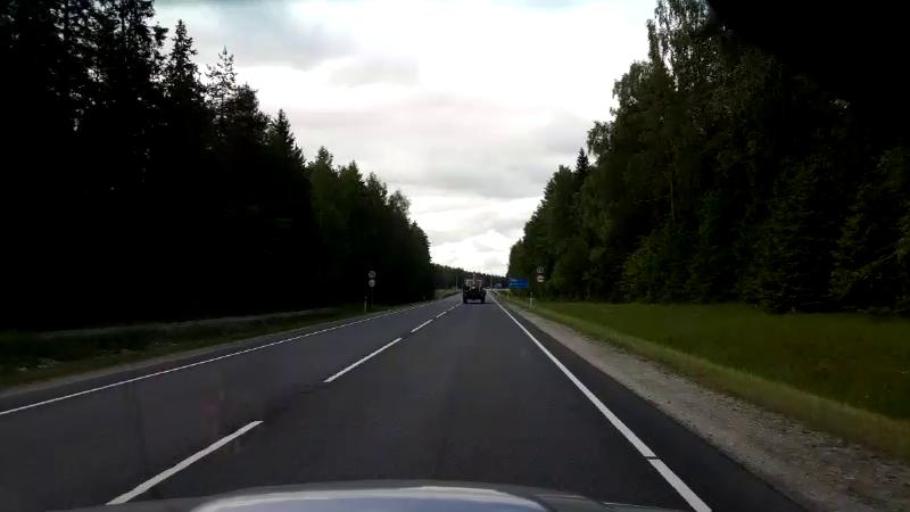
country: EE
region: Raplamaa
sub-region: Maerjamaa vald
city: Marjamaa
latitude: 58.8987
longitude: 24.4555
